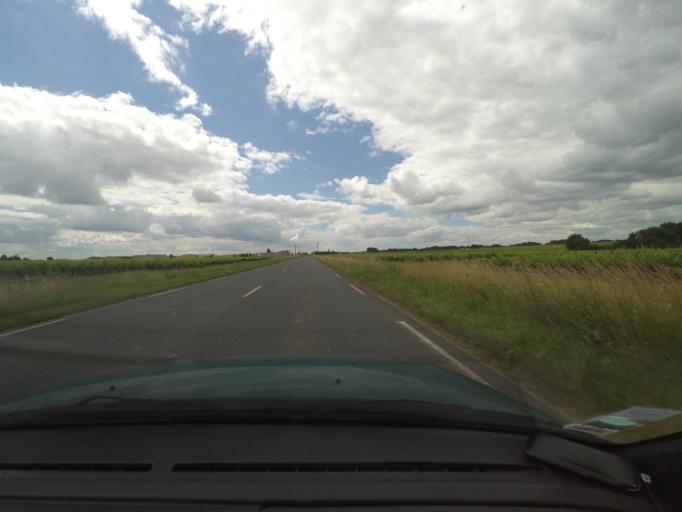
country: FR
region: Pays de la Loire
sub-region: Departement de la Loire-Atlantique
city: Mouzillon
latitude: 47.1303
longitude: -1.2826
